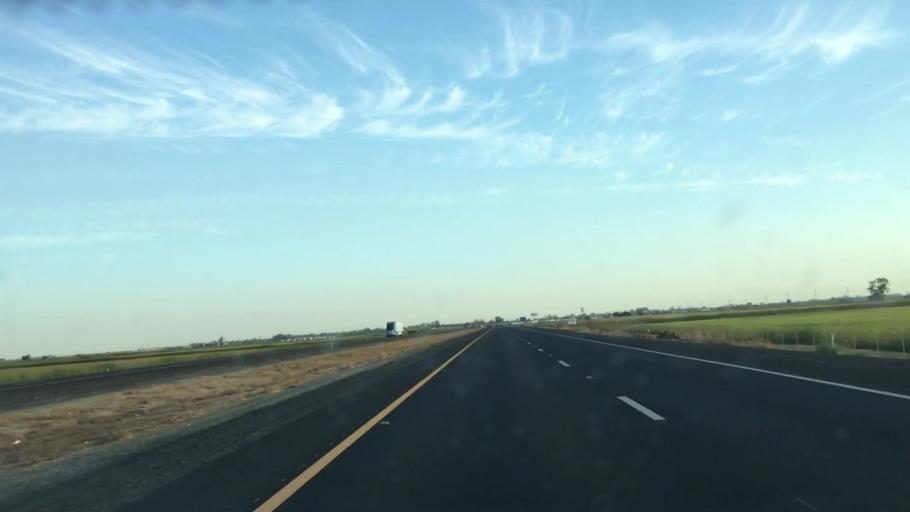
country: US
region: California
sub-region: Glenn County
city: Willows
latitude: 39.4777
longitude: -122.1957
